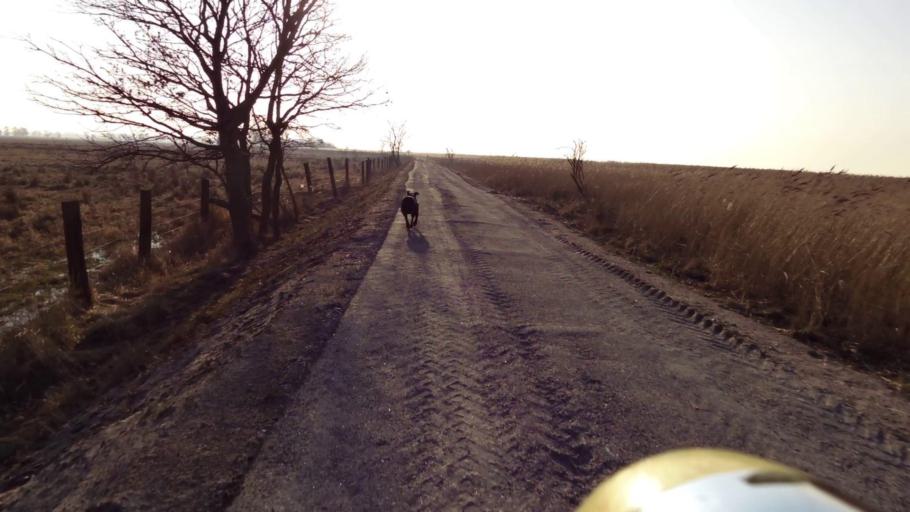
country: PL
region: West Pomeranian Voivodeship
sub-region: Powiat kamienski
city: Wolin
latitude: 53.7453
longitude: 14.5568
